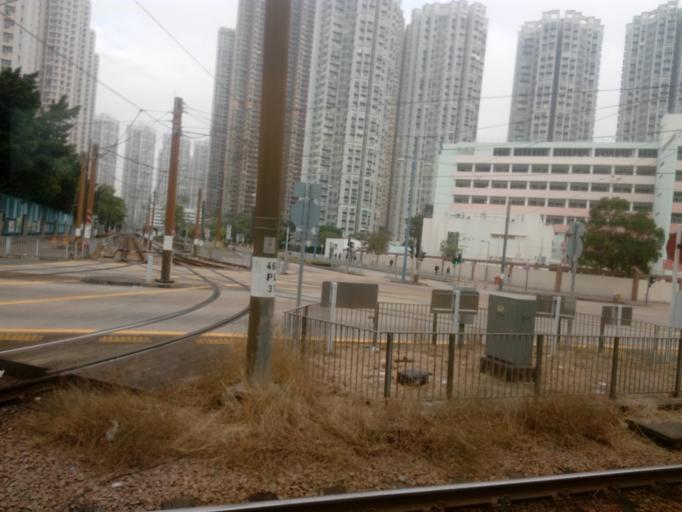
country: HK
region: Yuen Long
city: Yuen Long Kau Hui
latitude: 22.4587
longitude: 113.9980
